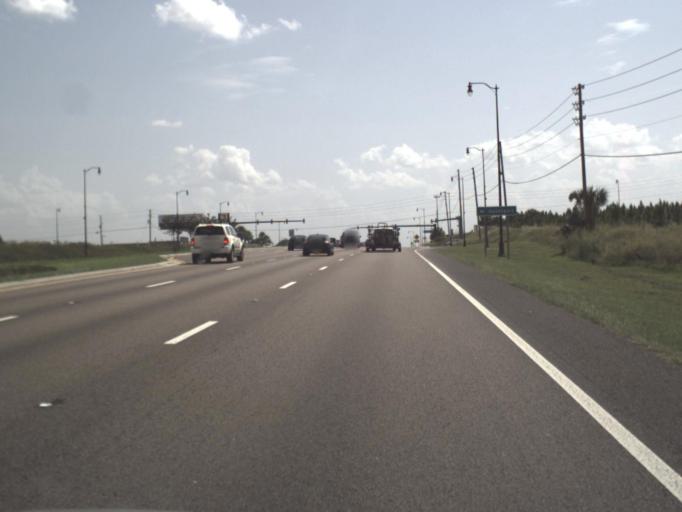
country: US
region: Florida
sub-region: Polk County
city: Davenport
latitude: 28.1601
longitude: -81.6399
